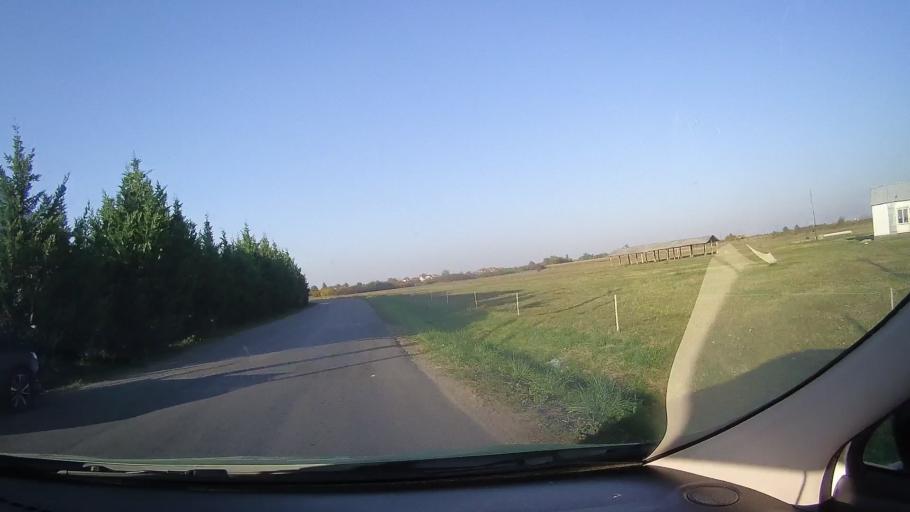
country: RO
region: Bihor
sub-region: Comuna Bors
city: Bors
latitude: 47.1097
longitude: 21.8239
